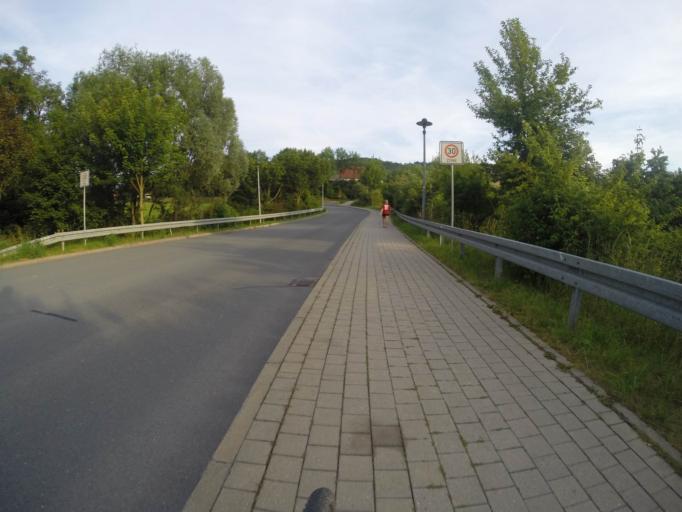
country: DE
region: Thuringia
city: Jena
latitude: 50.9335
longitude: 11.6237
